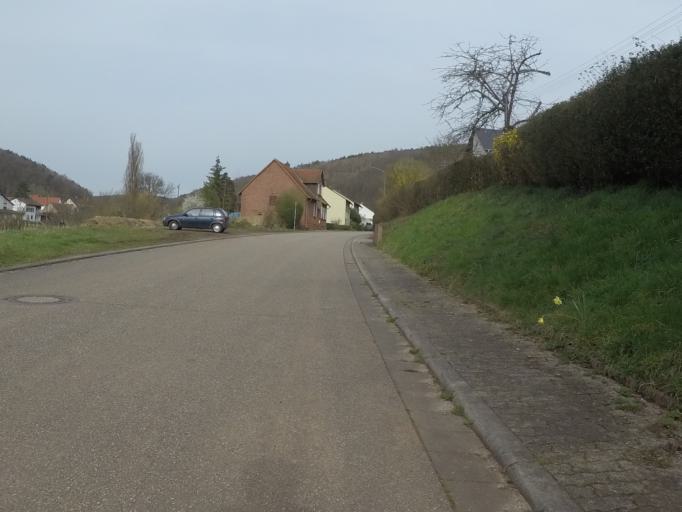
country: DE
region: Rheinland-Pfalz
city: Waldrohrbach
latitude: 49.1678
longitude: 7.9704
